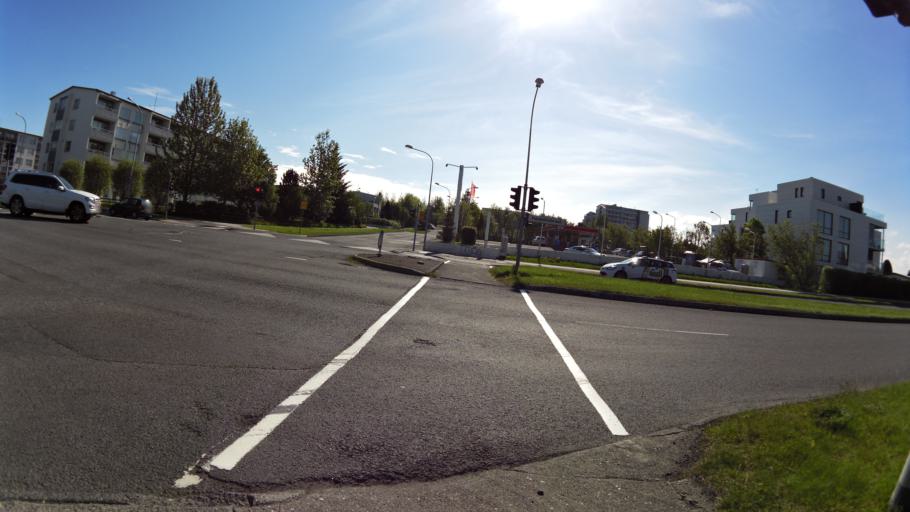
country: IS
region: Capital Region
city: Reykjavik
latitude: 64.1266
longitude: -21.8878
